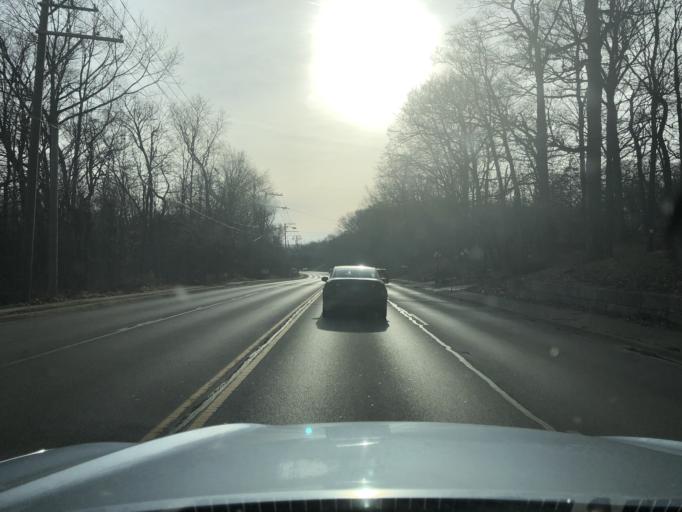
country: US
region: Illinois
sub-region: DuPage County
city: Bloomingdale
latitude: 41.9654
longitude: -88.0812
